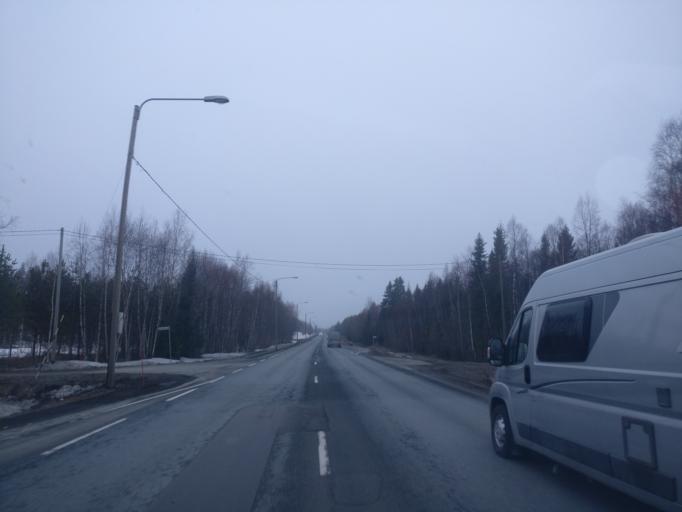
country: FI
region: Lapland
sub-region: Kemi-Tornio
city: Simo
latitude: 65.6747
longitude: 24.8535
